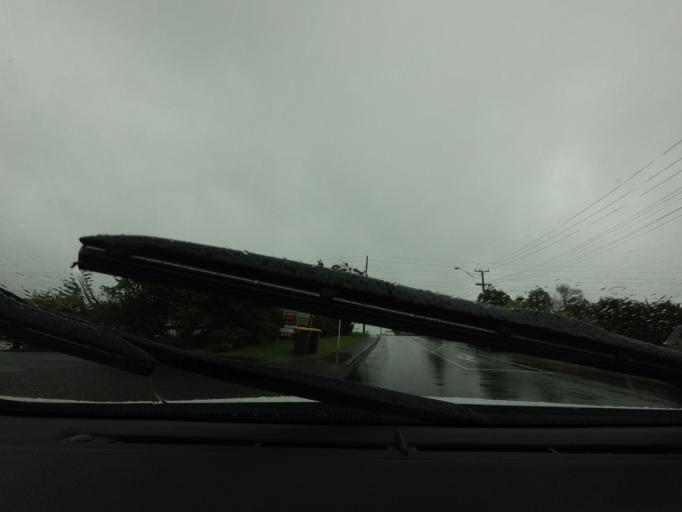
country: NZ
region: Auckland
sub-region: Auckland
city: Rothesay Bay
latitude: -36.7631
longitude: 174.7360
